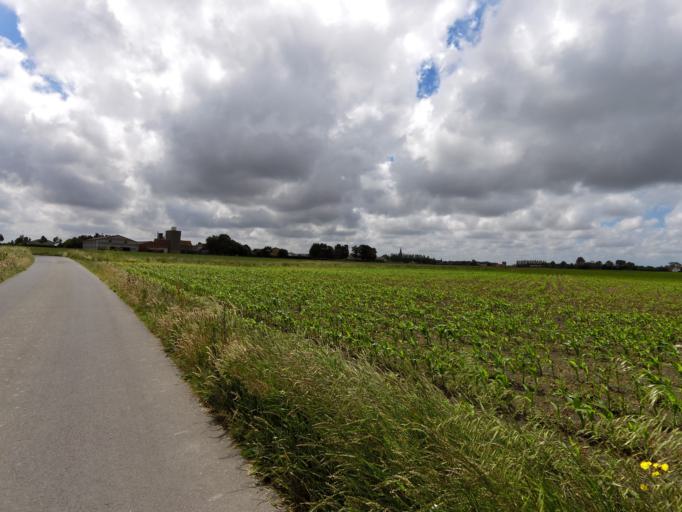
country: BE
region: Flanders
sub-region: Provincie West-Vlaanderen
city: Gistel
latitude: 51.1418
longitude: 2.9278
